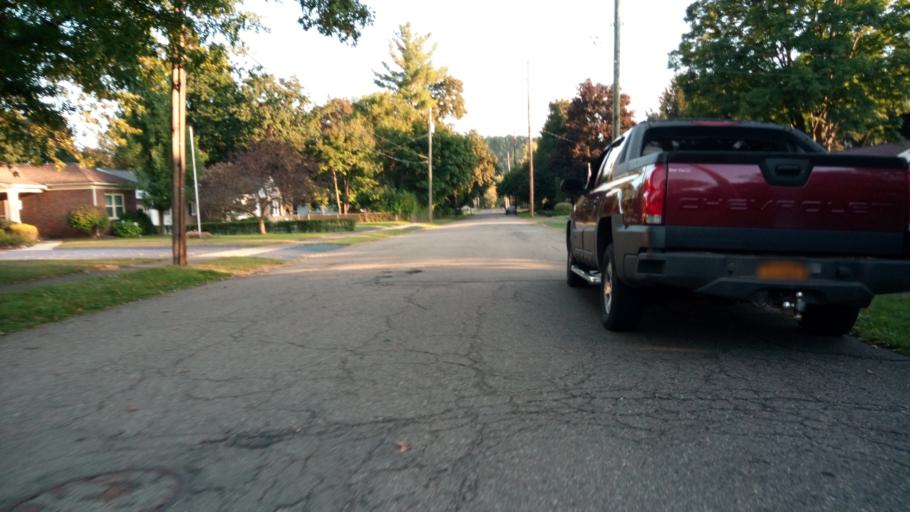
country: US
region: New York
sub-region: Chemung County
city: West Elmira
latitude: 42.0806
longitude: -76.8374
